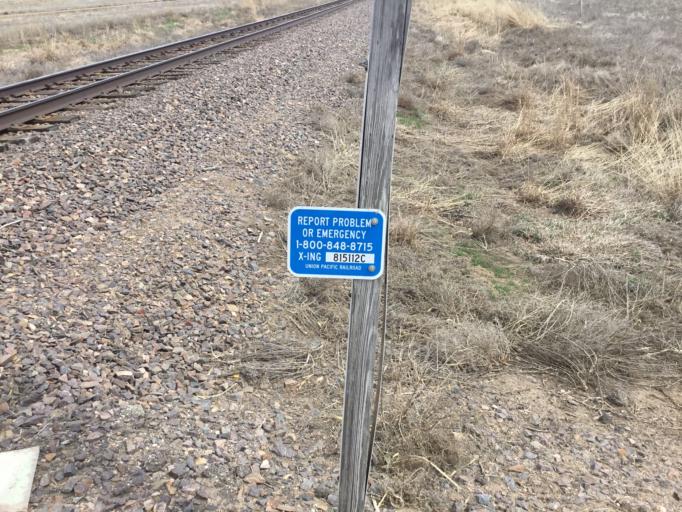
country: US
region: Kansas
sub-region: Trego County
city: WaKeeney
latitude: 39.0296
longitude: -99.9270
